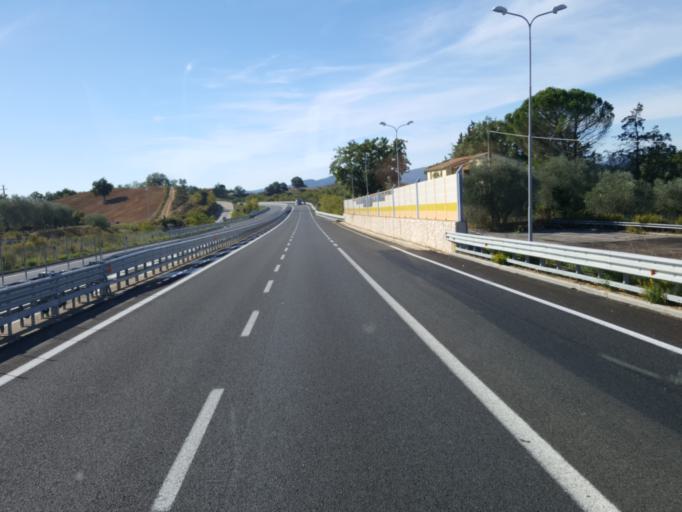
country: IT
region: Tuscany
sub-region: Provincia di Grosseto
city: Civitella Marittima
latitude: 42.9765
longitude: 11.2821
